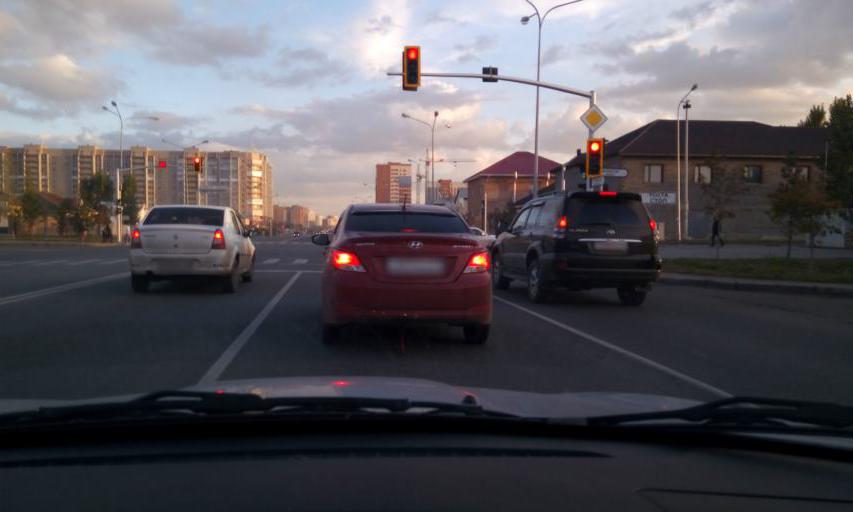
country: KZ
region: Astana Qalasy
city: Astana
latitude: 51.1343
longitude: 71.4934
